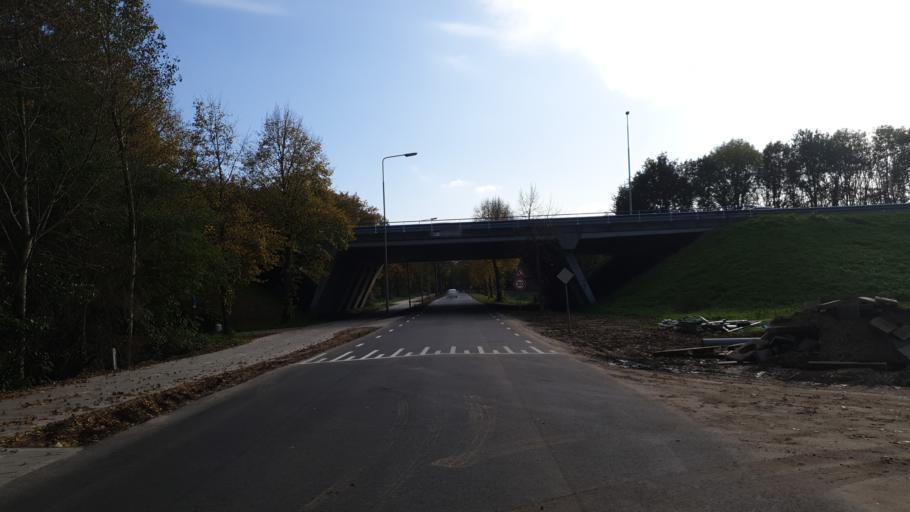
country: NL
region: Limburg
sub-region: Gemeente Gennep
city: Gennep
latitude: 51.6665
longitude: 5.9830
